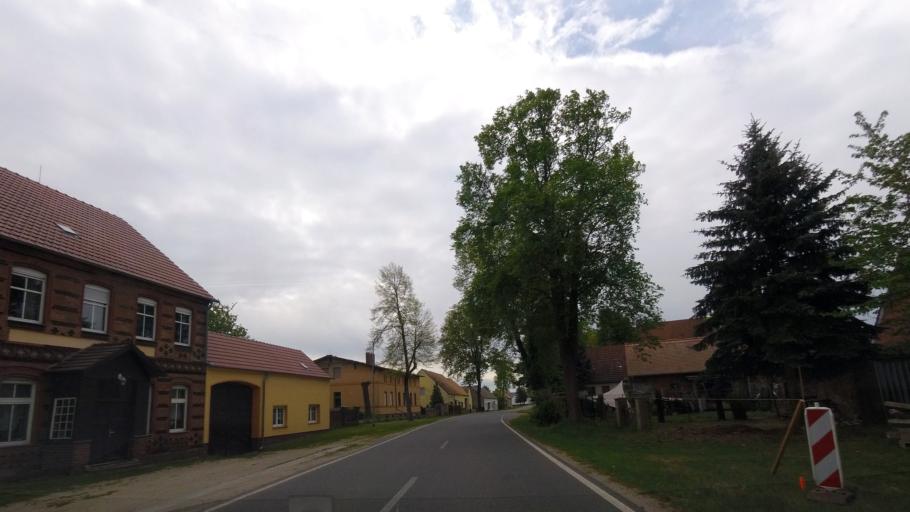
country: DE
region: Brandenburg
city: Dahme
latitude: 51.8985
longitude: 13.4085
